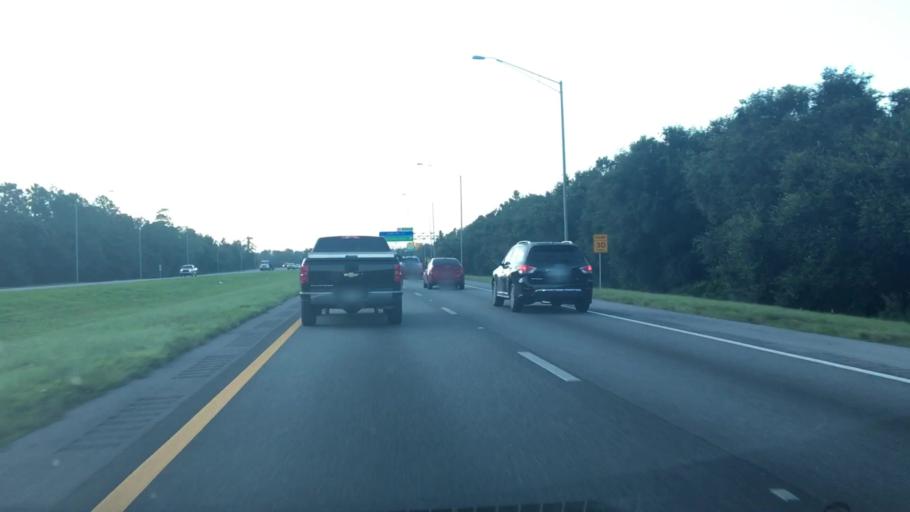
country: US
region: Florida
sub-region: Seminole County
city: Goldenrod
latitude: 28.6038
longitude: -81.2540
